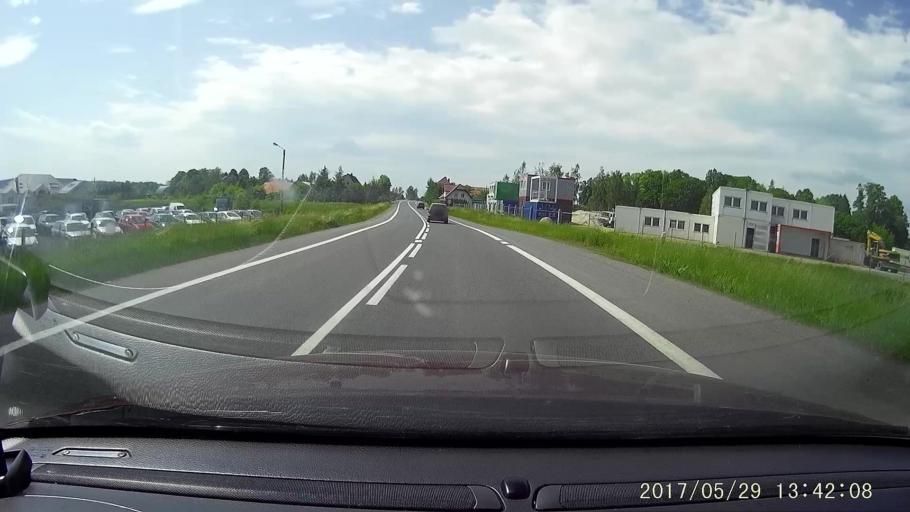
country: PL
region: Lower Silesian Voivodeship
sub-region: Powiat lubanski
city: Pisarzowice
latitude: 51.1370
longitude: 15.2428
